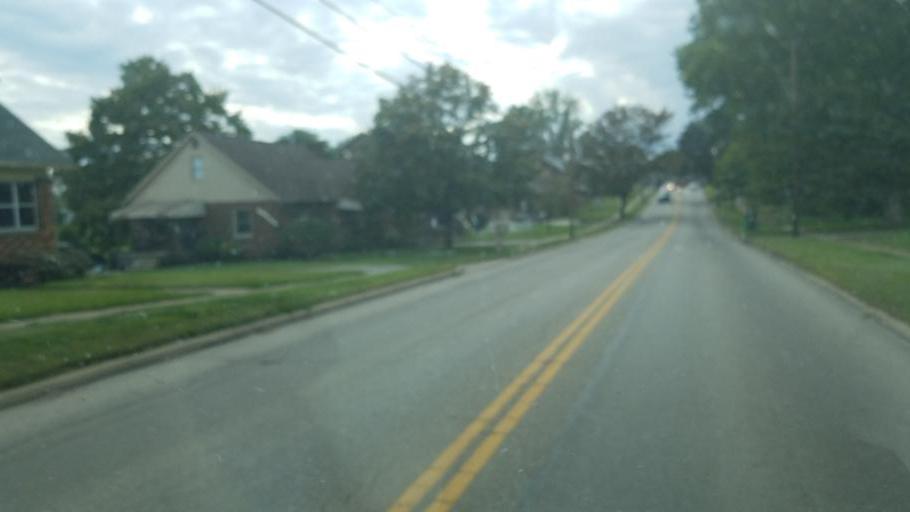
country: US
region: Ohio
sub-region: Tuscarawas County
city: Sugarcreek
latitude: 40.5083
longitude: -81.6351
